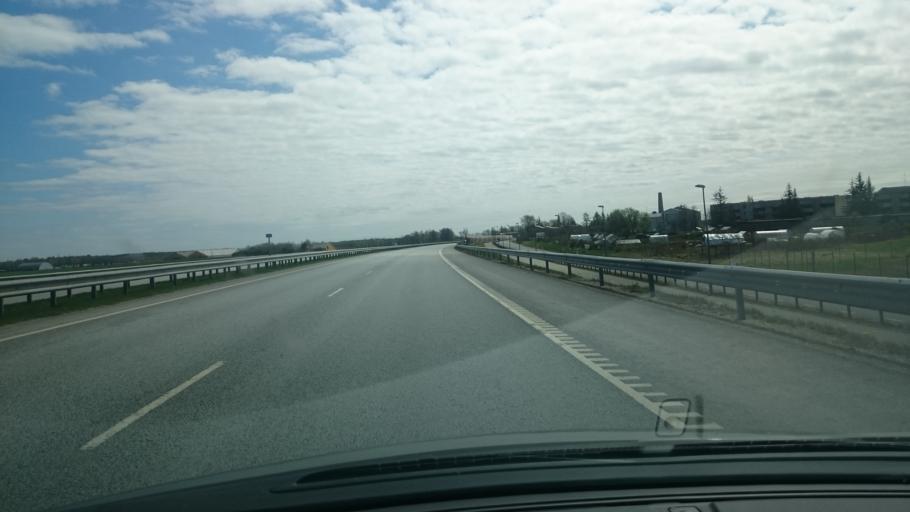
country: EE
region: Ida-Virumaa
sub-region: Johvi vald
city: Johvi
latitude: 59.3812
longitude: 27.3682
